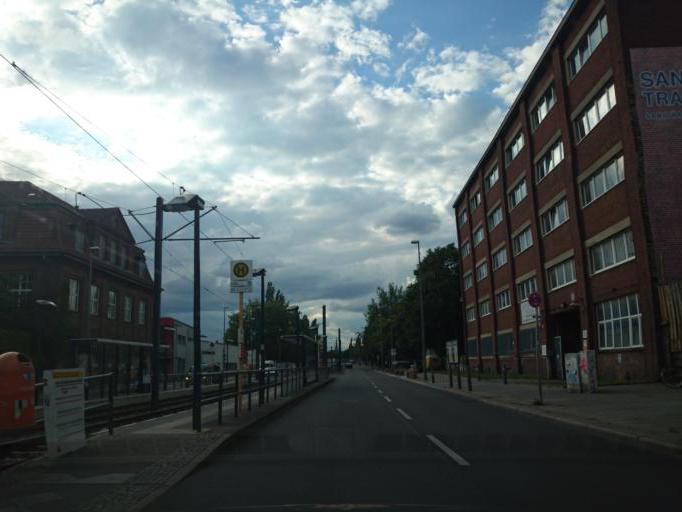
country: DE
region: Berlin
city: Rummelsburg
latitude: 52.4931
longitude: 13.4909
